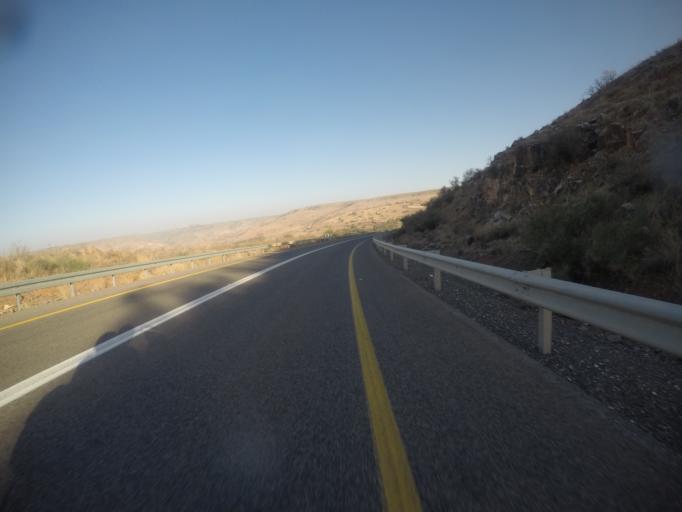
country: SY
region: Quneitra
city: Fiq
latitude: 32.8139
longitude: 35.6760
